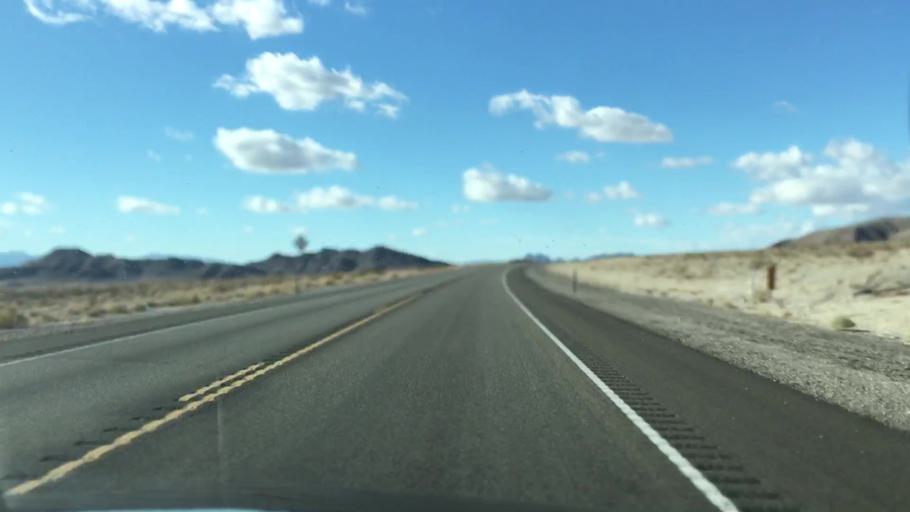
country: US
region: Nevada
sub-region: Nye County
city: Pahrump
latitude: 36.5729
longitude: -116.1819
